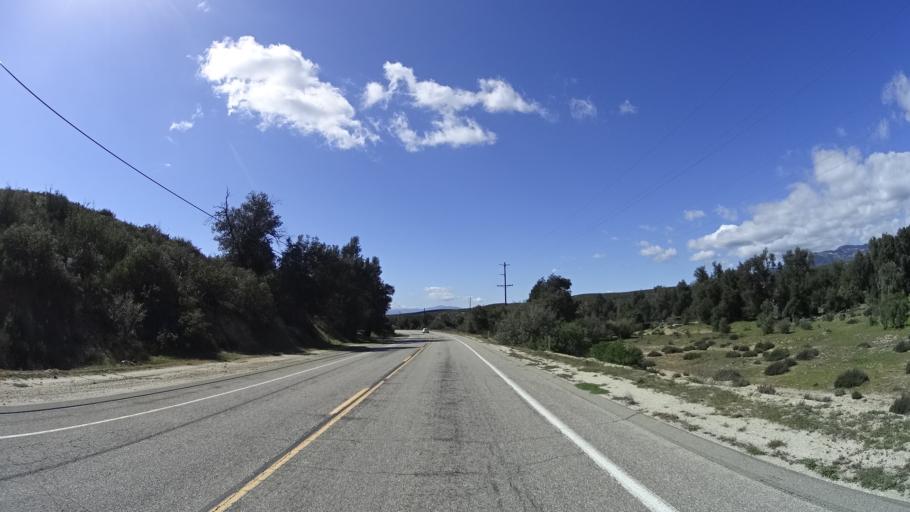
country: US
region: California
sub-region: San Diego County
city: Julian
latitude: 33.2171
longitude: -116.5725
